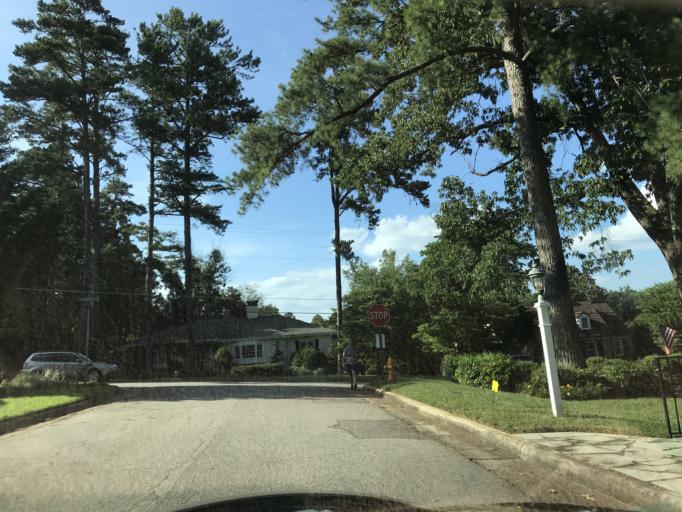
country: US
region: North Carolina
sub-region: Wake County
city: West Raleigh
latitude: 35.8079
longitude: -78.6681
